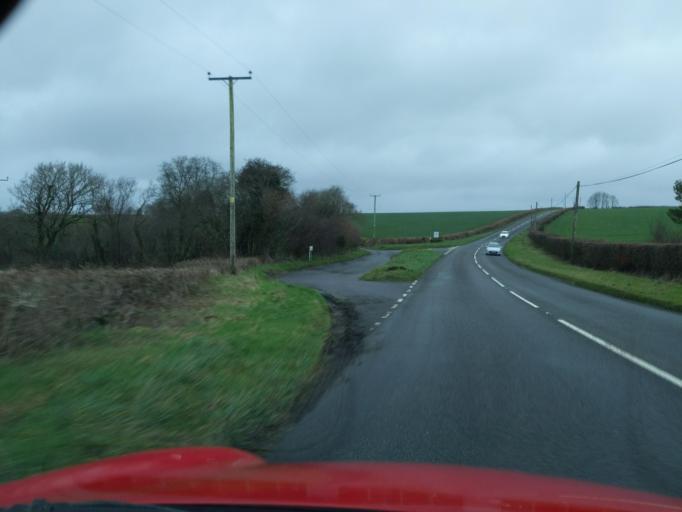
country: GB
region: England
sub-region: Cornwall
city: Boyton
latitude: 50.7174
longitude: -4.3292
